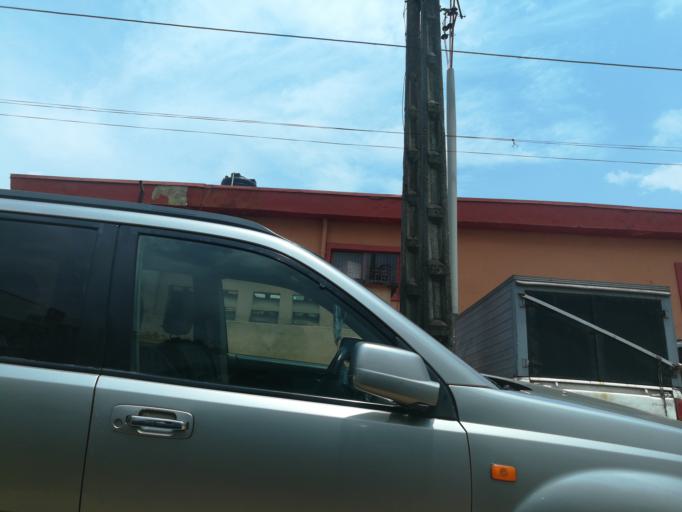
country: NG
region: Lagos
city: Oshodi
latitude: 6.5493
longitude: 3.3318
